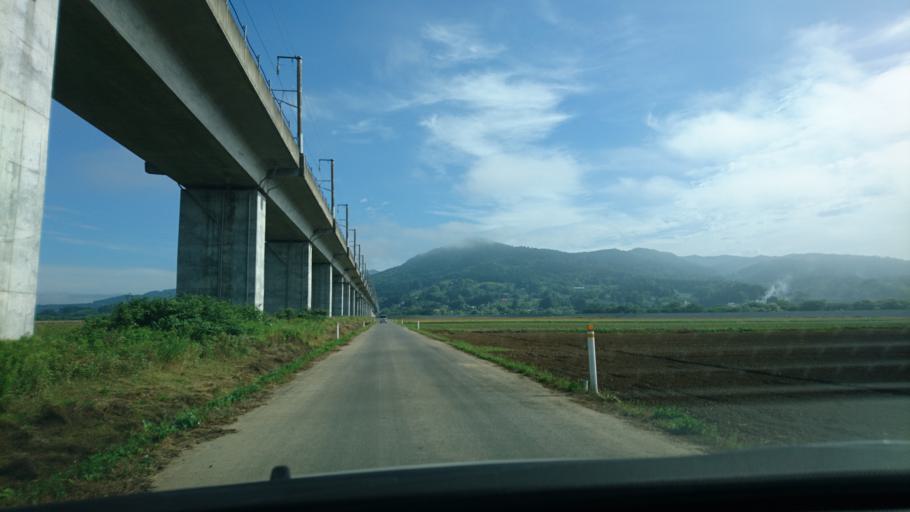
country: JP
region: Iwate
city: Ichinoseki
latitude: 38.9654
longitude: 141.1533
